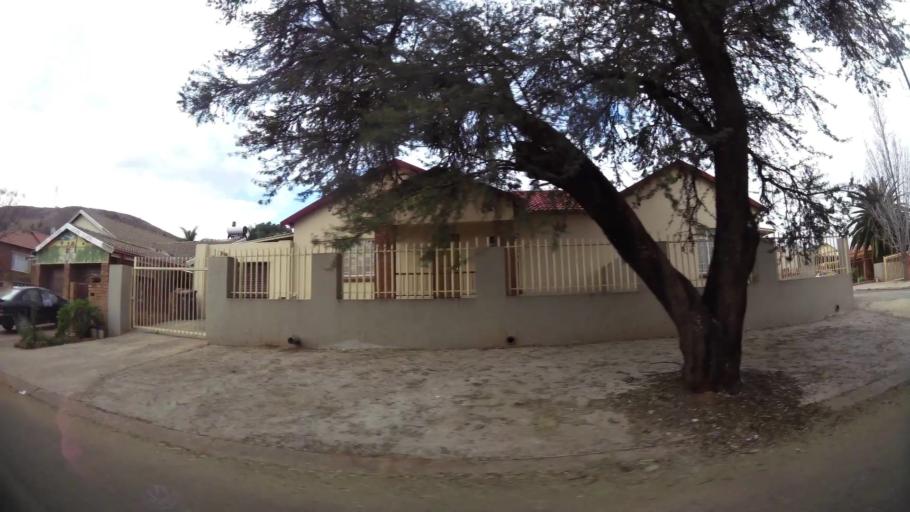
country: ZA
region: Gauteng
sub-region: City of Tshwane Metropolitan Municipality
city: Pretoria
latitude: -25.6985
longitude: 28.2992
